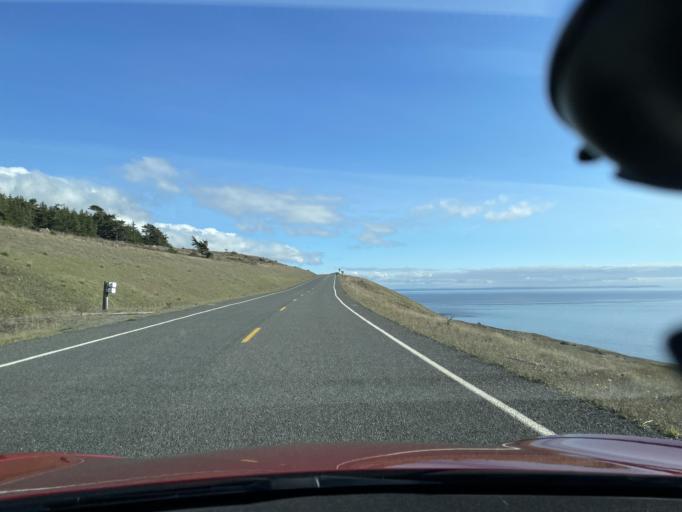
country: US
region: Washington
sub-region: San Juan County
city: Friday Harbor
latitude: 48.4565
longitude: -122.9803
